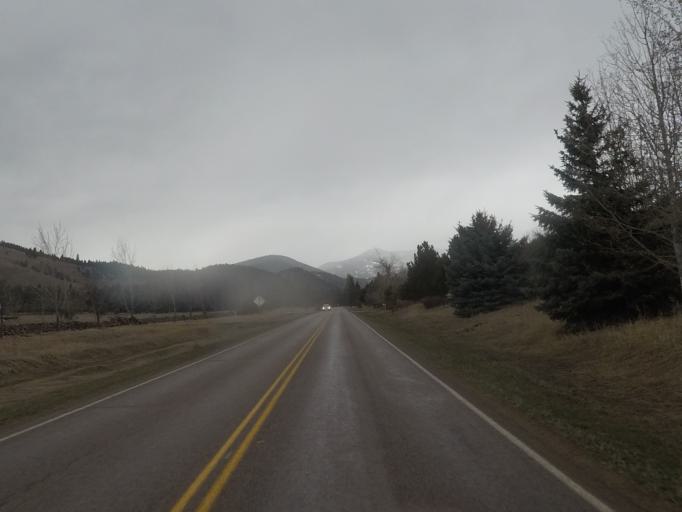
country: US
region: Montana
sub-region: Missoula County
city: East Missoula
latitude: 46.9028
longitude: -113.9604
